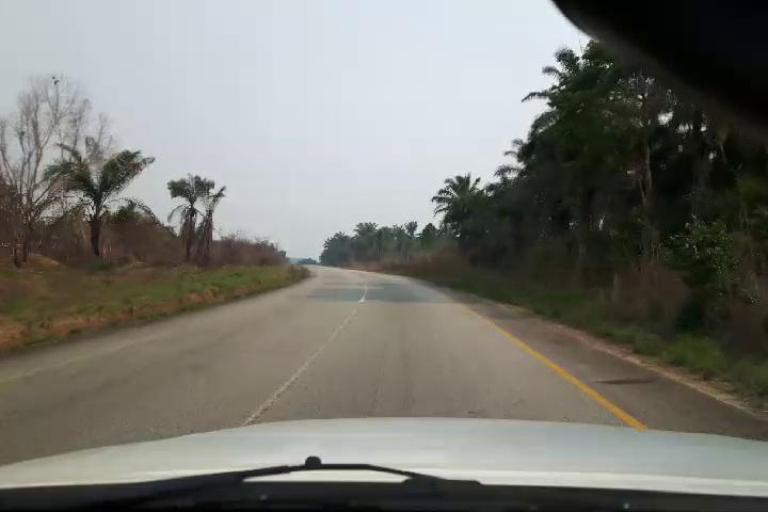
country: SL
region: Southern Province
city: Largo
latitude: 8.2141
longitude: -12.0733
